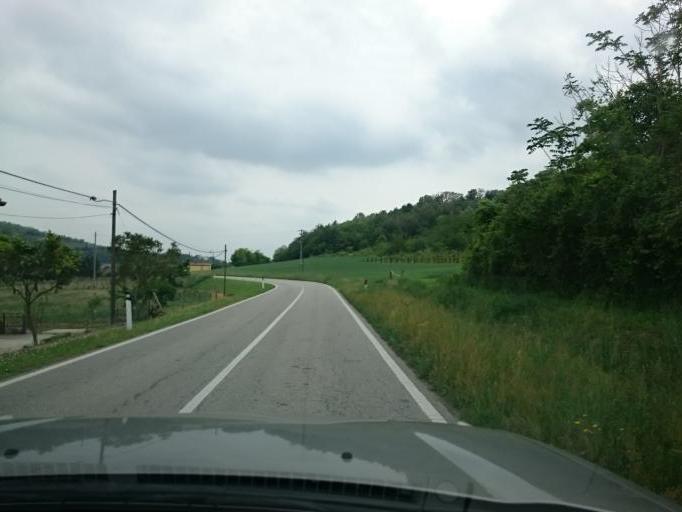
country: IT
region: Veneto
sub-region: Provincia di Padova
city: Arqua Petrarca
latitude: 45.2647
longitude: 11.7201
